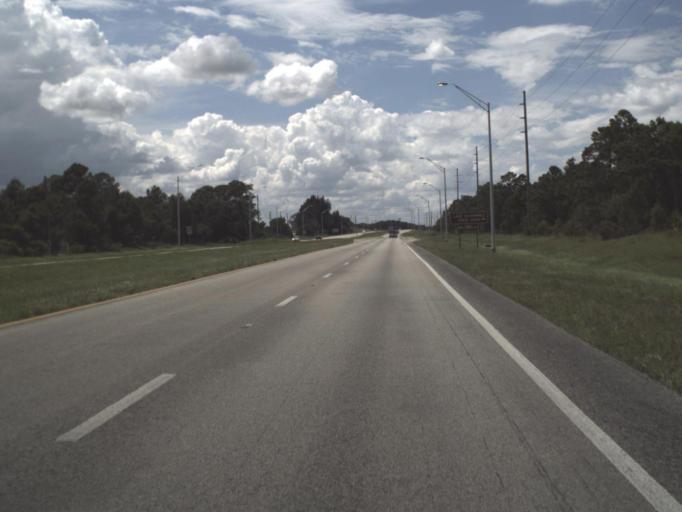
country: US
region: Florida
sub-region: Polk County
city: Babson Park
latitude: 27.8827
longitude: -81.4452
